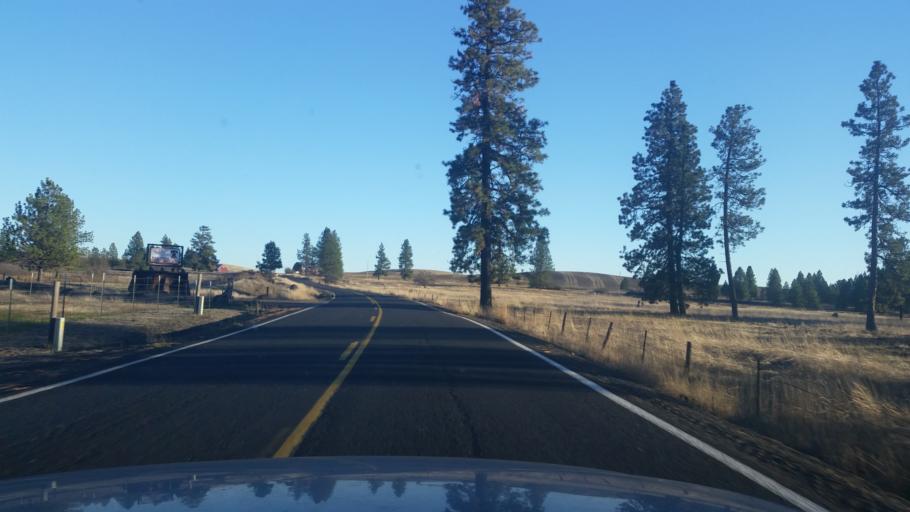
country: US
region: Washington
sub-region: Spokane County
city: Opportunity
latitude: 47.3790
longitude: -117.3108
